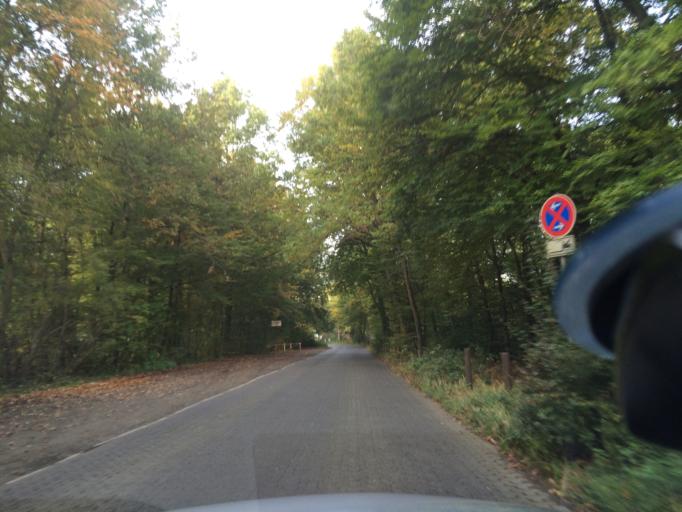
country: DE
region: Hesse
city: Morfelden-Walldorf
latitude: 49.9695
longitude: 8.5501
